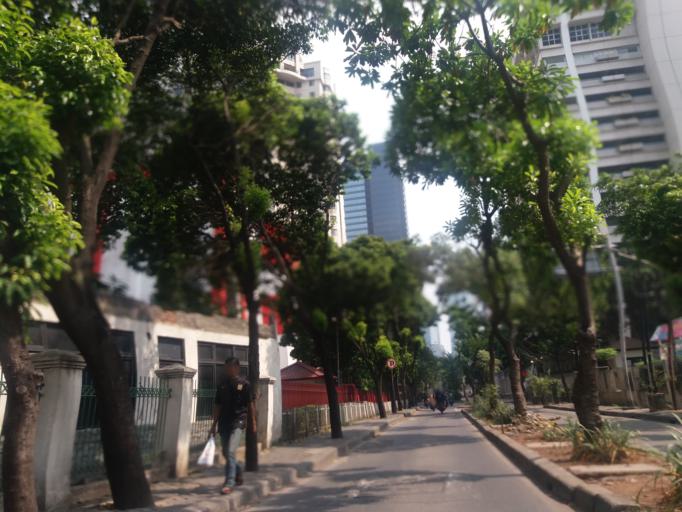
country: ID
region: Jakarta Raya
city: Jakarta
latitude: -6.2188
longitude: 106.8168
